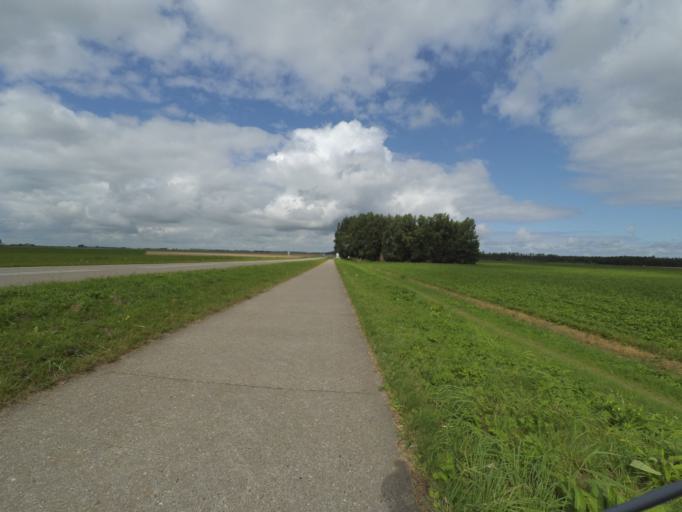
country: NL
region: Groningen
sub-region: Gemeente Zuidhorn
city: Grijpskerk
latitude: 53.3156
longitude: 6.2615
